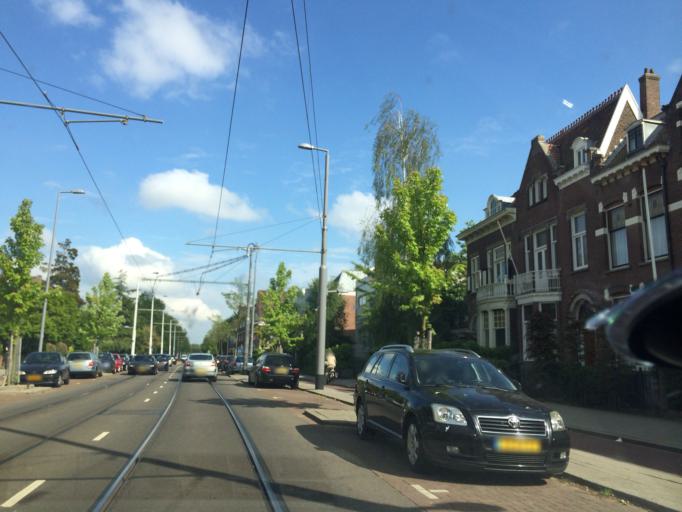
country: NL
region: South Holland
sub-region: Gemeente Rotterdam
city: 's-Gravenland
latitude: 51.9242
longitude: 4.5168
